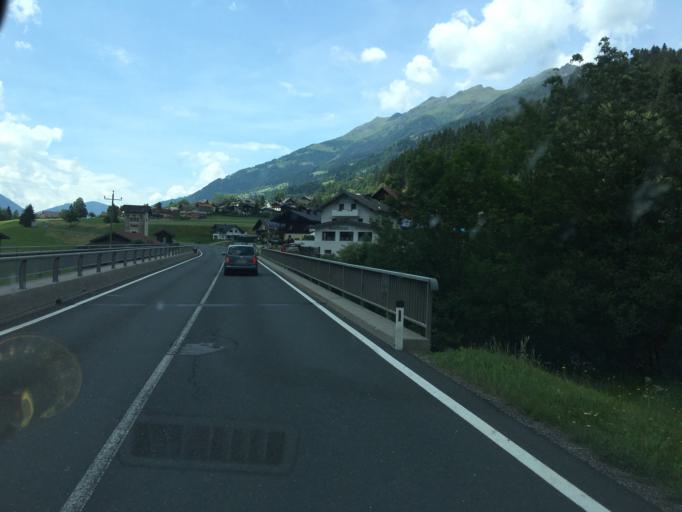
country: AT
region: Carinthia
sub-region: Politischer Bezirk Spittal an der Drau
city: Stall
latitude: 46.8882
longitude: 13.0452
